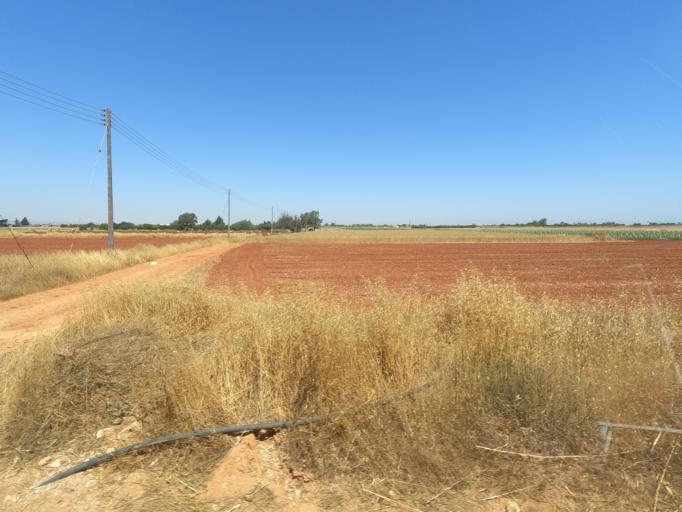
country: CY
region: Ammochostos
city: Liopetri
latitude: 35.0252
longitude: 33.8833
